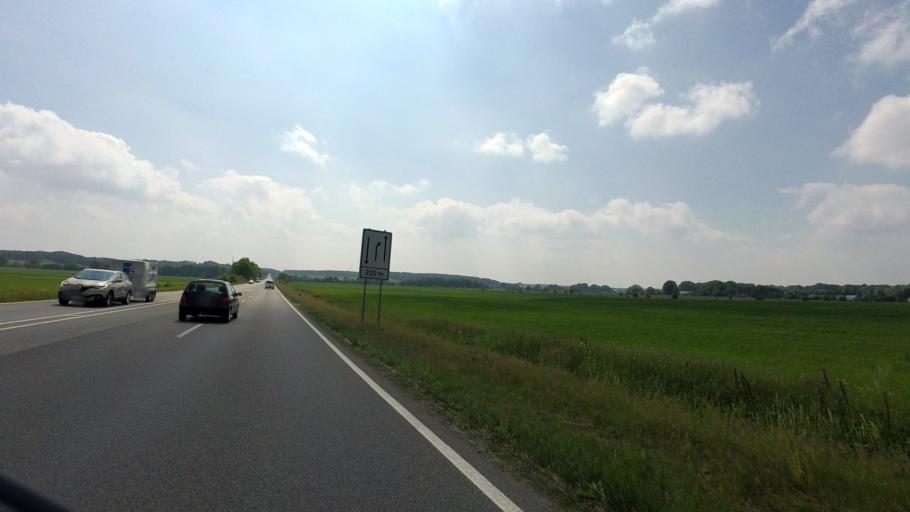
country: DE
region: Brandenburg
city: Cottbus
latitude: 51.6698
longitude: 14.3571
